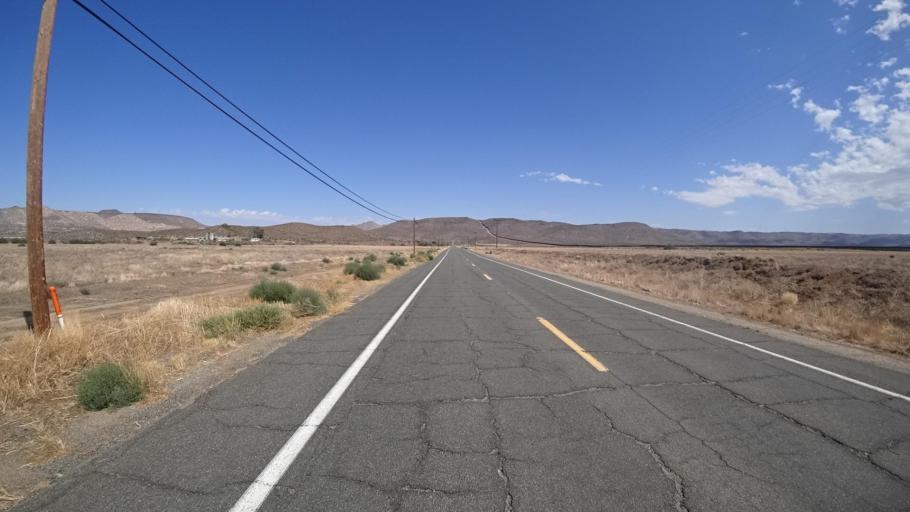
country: MX
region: Baja California
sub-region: Tecate
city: Cereso del Hongo
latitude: 32.6177
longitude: -116.1761
